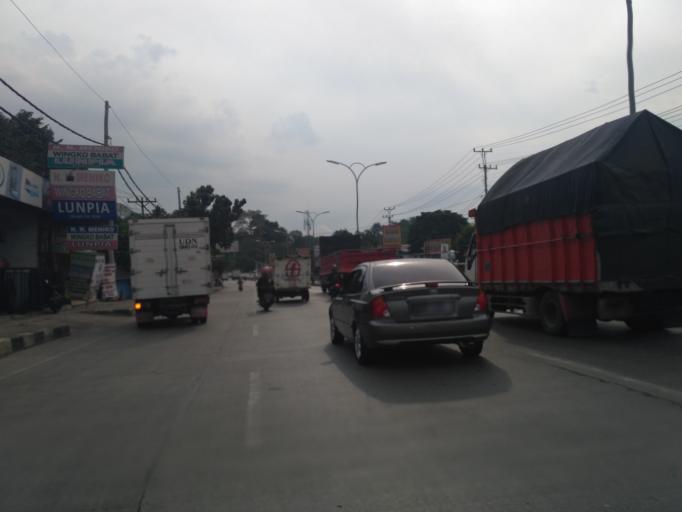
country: ID
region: Central Java
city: Semarang
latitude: -6.9829
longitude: 110.3532
